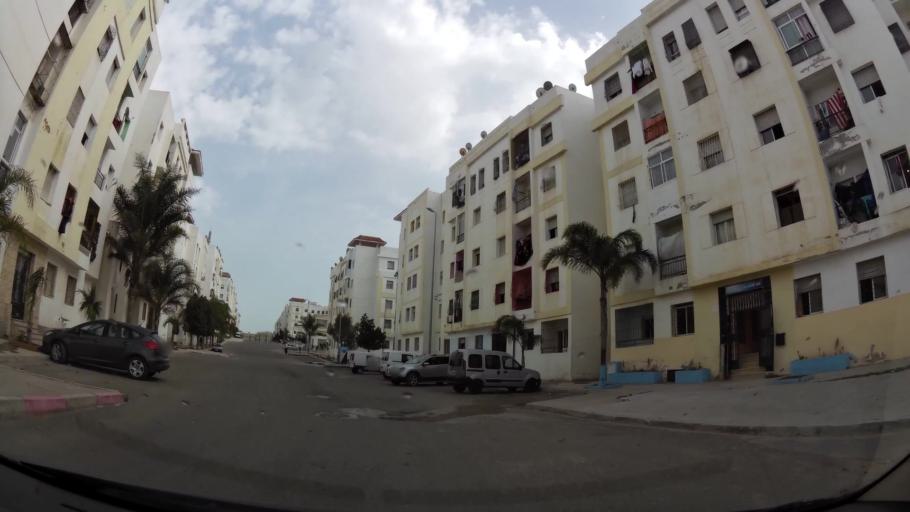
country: MA
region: Tanger-Tetouan
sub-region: Tanger-Assilah
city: Boukhalef
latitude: 35.7393
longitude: -5.8905
